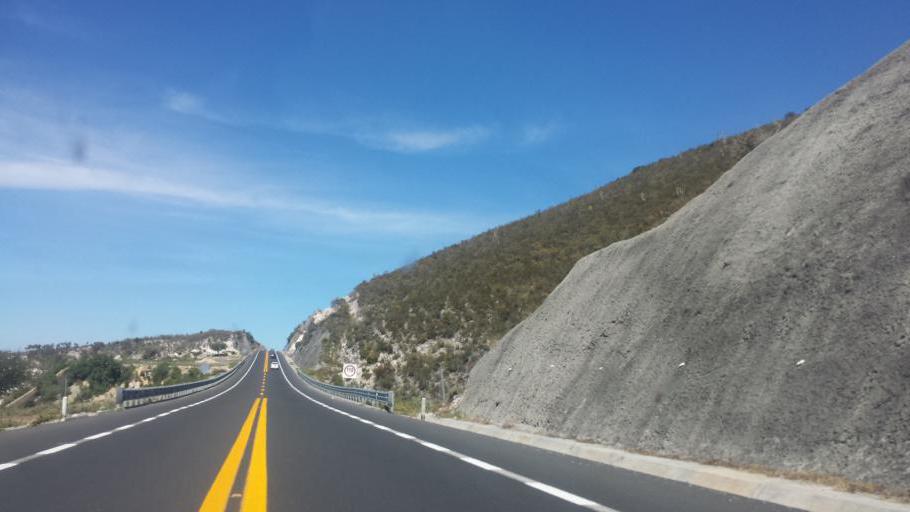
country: MX
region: Puebla
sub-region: San Jose Miahuatlan
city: San Pedro Tetitlan
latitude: 18.0025
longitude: -97.3553
